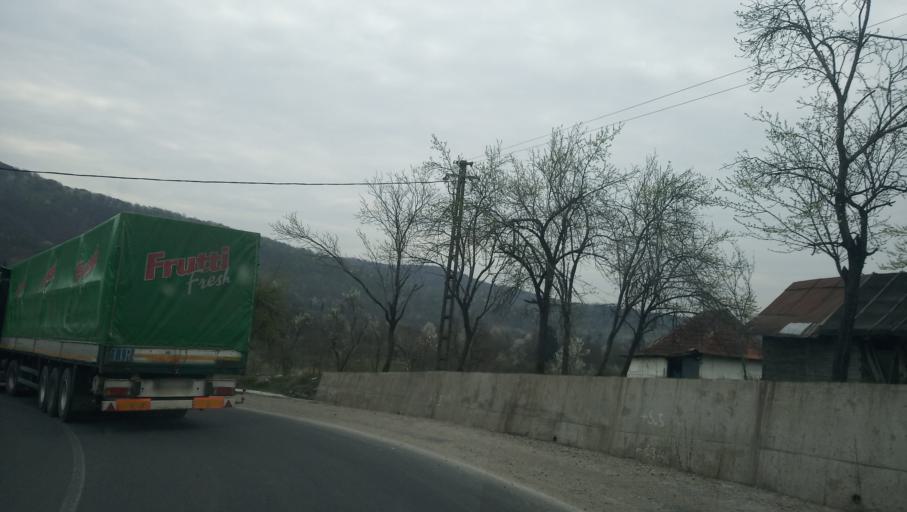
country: RO
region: Arad
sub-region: Comuna Varfurile
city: Varfurile
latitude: 46.3427
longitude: 22.5537
